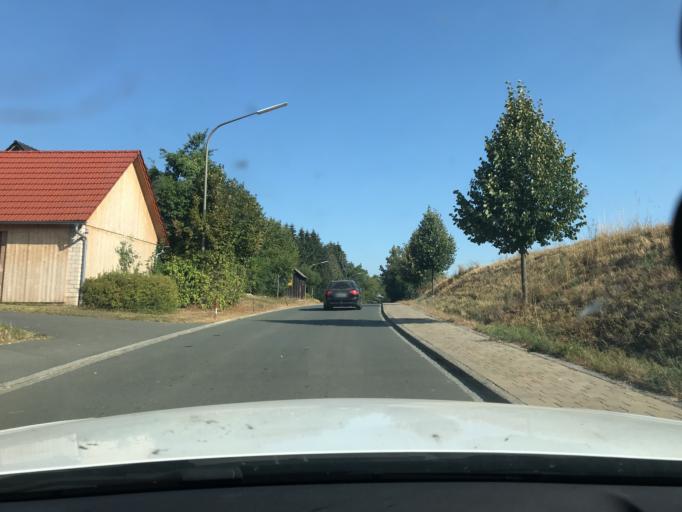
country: DE
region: Bavaria
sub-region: Upper Franconia
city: Pegnitz
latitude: 49.7813
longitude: 11.5785
